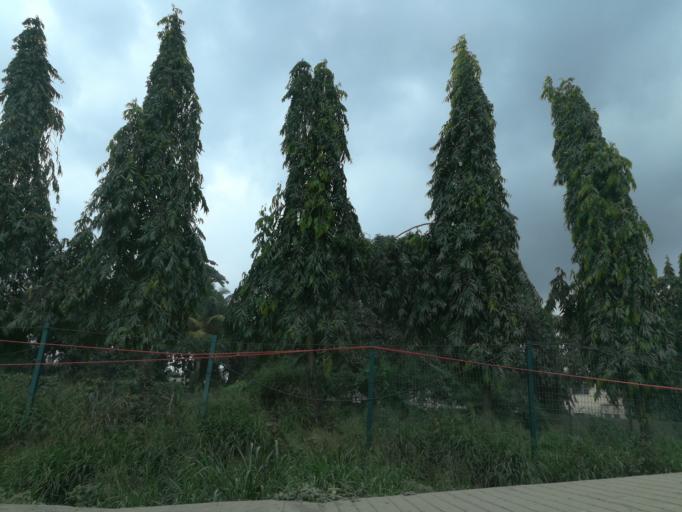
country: NG
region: Lagos
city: Oshodi
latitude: 6.5712
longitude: 3.3456
